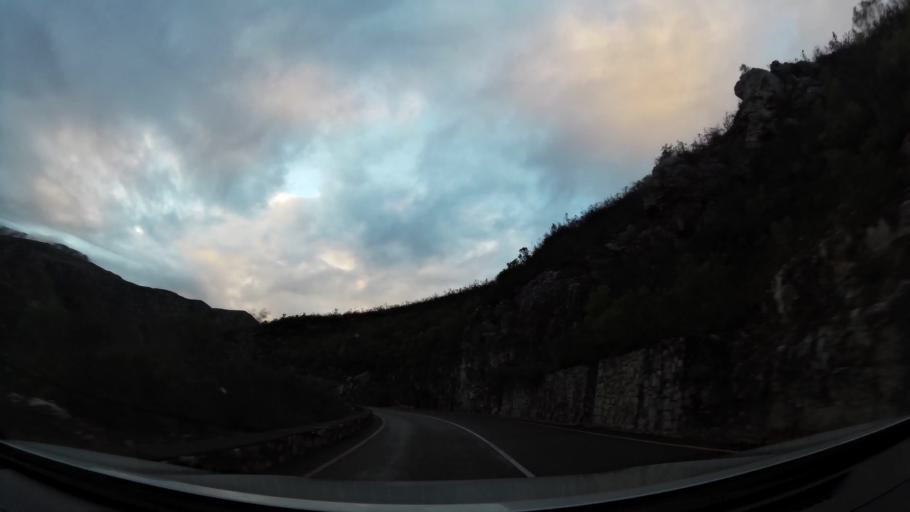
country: ZA
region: Western Cape
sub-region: Overberg District Municipality
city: Swellendam
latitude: -33.9841
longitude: 20.7102
